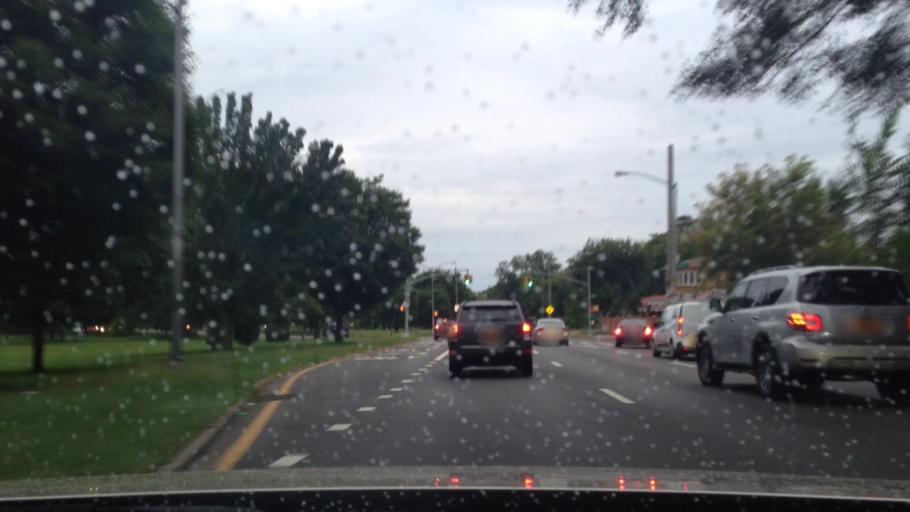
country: US
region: New York
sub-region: Kings County
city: East New York
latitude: 40.6746
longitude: -73.8628
